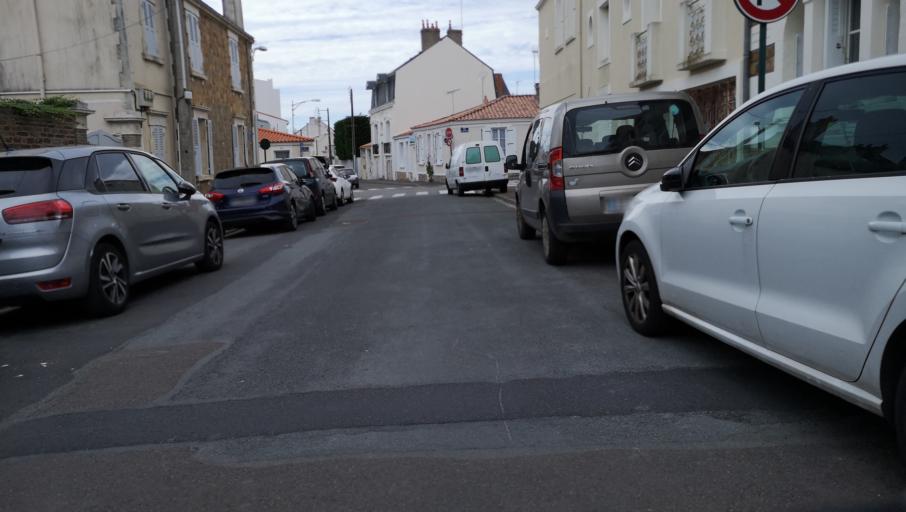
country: FR
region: Pays de la Loire
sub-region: Departement de la Vendee
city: Les Sables-d'Olonne
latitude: 46.4921
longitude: -1.7711
